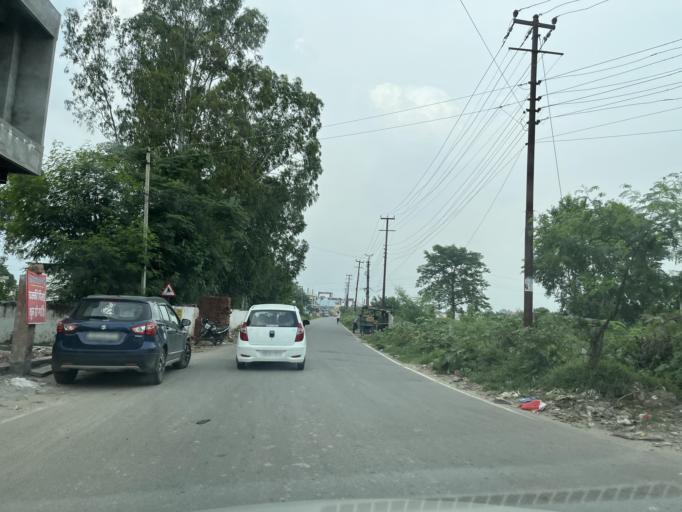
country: IN
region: Uttarakhand
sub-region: Naini Tal
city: Haldwani
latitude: 29.1899
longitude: 79.4791
